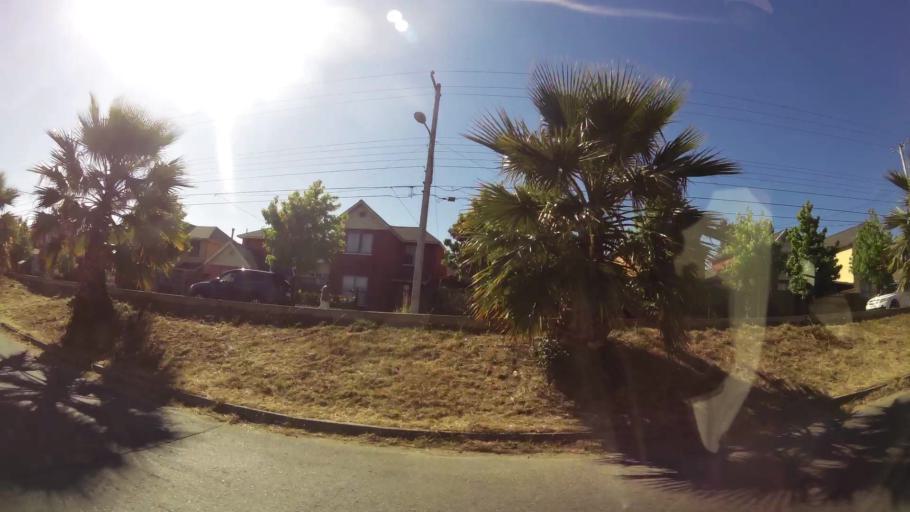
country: CL
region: Valparaiso
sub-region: Provincia de Valparaiso
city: Vina del Mar
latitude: -33.1268
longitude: -71.5655
